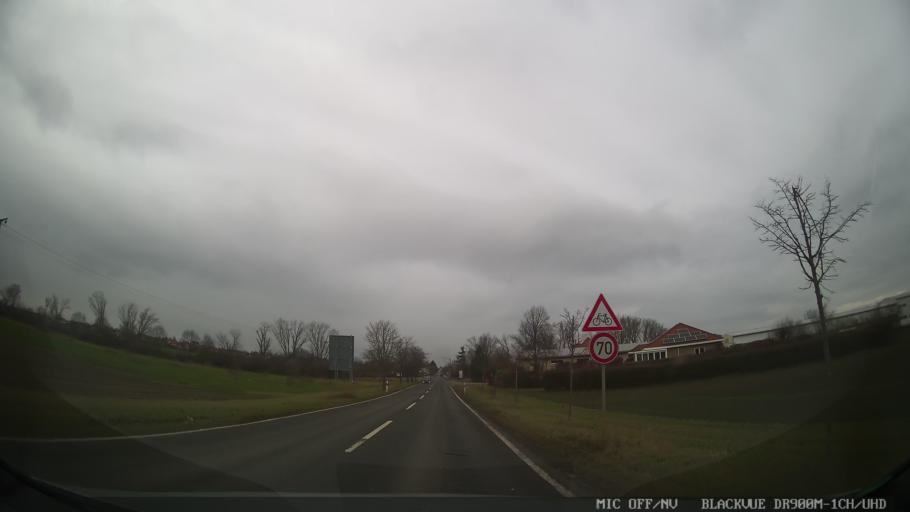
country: DE
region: Rheinland-Pfalz
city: Gau-Odernheim
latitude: 49.7762
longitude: 8.2017
